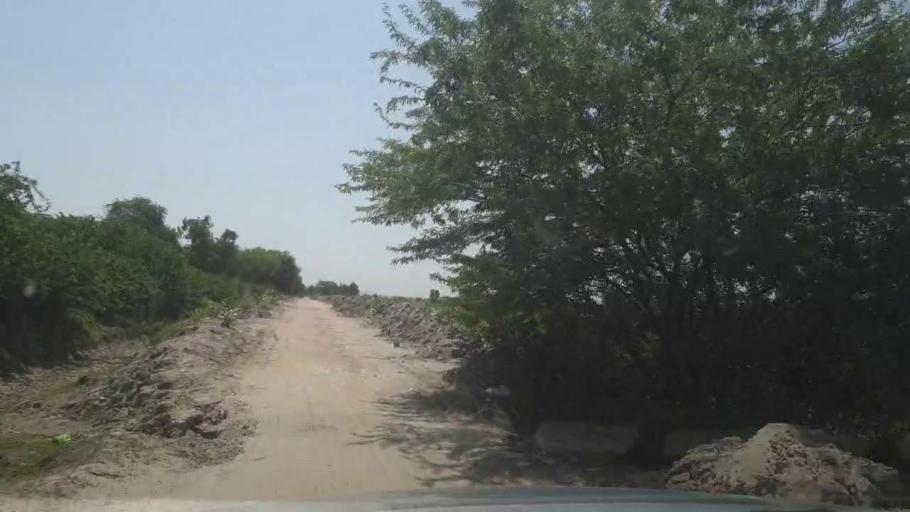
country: PK
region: Sindh
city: Khairpur
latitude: 27.3541
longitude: 69.0424
